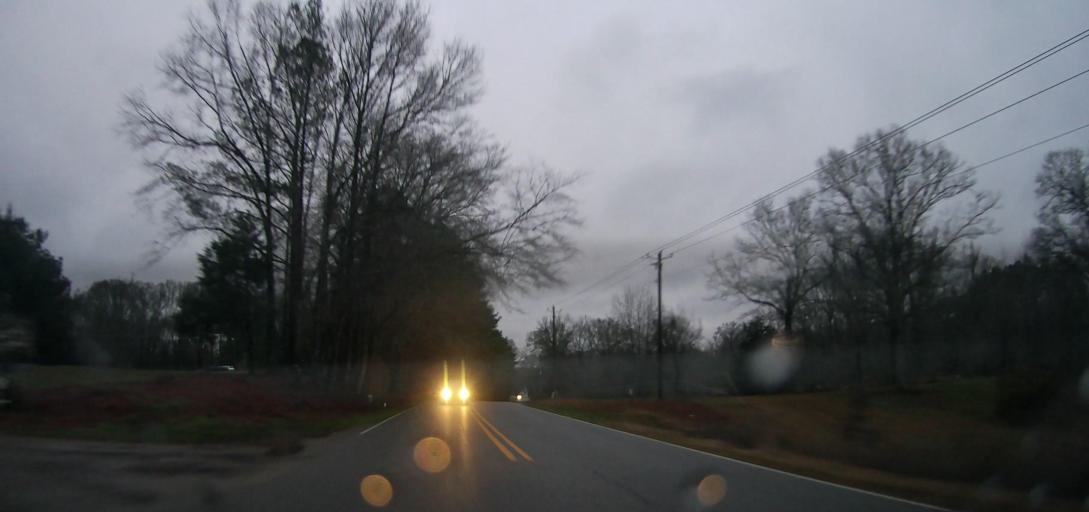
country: US
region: Alabama
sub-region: Tuscaloosa County
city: Vance
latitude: 33.1194
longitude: -87.2234
